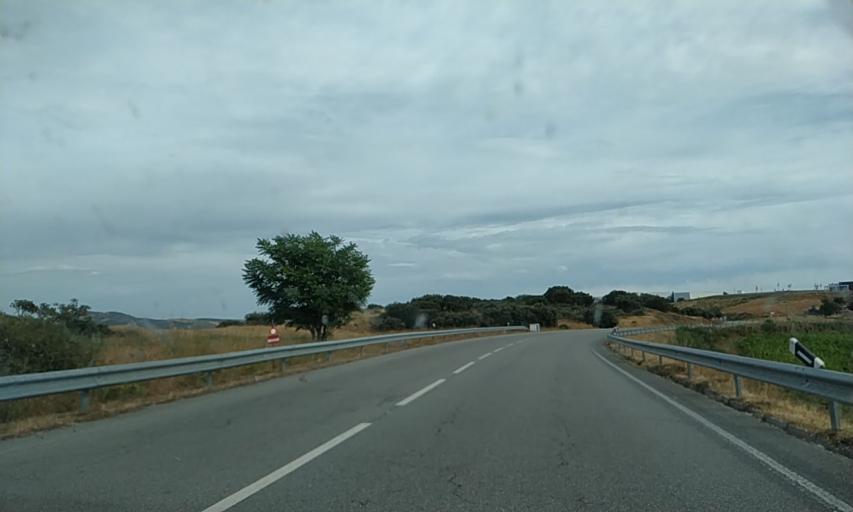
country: PT
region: Viseu
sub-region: Sao Joao da Pesqueira
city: Sao Joao da Pesqueira
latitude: 41.1221
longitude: -7.3904
